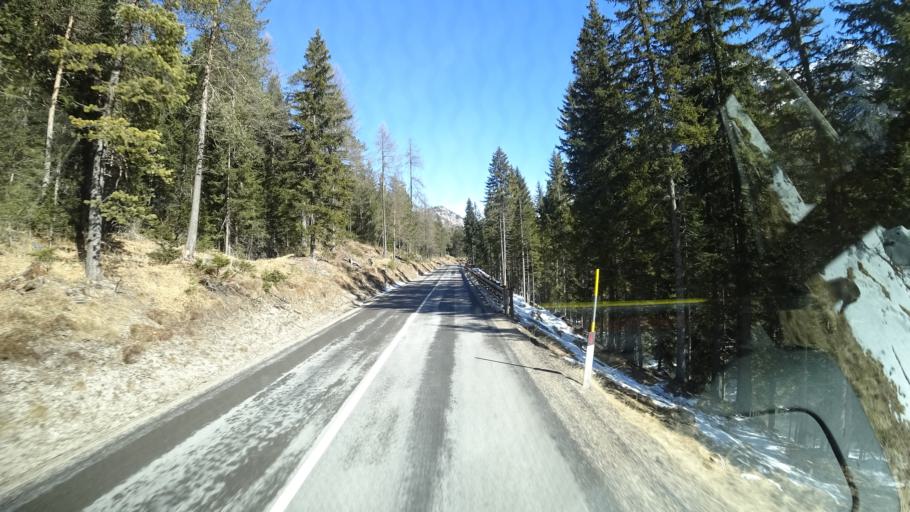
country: IT
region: Veneto
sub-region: Provincia di Belluno
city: Cortina d'Ampezzo
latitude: 46.6056
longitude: 12.1480
